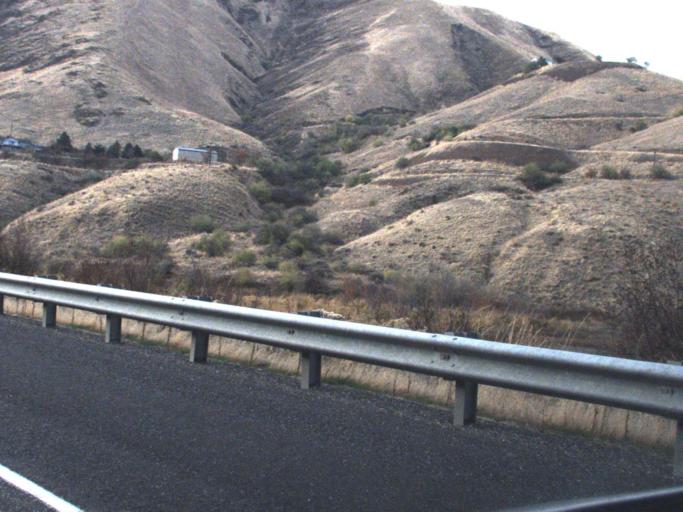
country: US
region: Washington
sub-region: Asotin County
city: Clarkston Heights-Vineland
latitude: 46.4149
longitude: -117.2081
